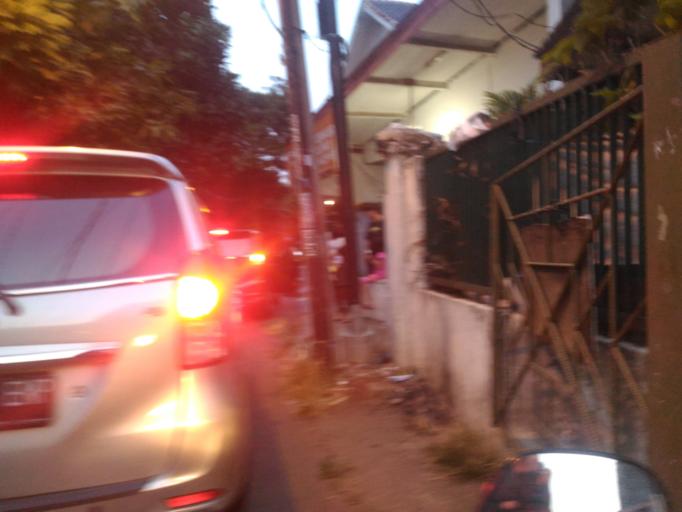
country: ID
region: West Java
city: Depok
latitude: -6.3630
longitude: 106.8356
